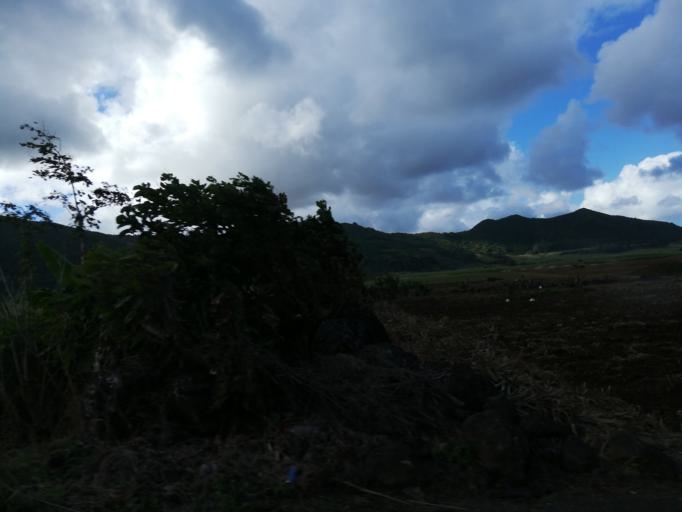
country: MU
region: Flacq
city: Clemencia
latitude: -20.2602
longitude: 57.7029
